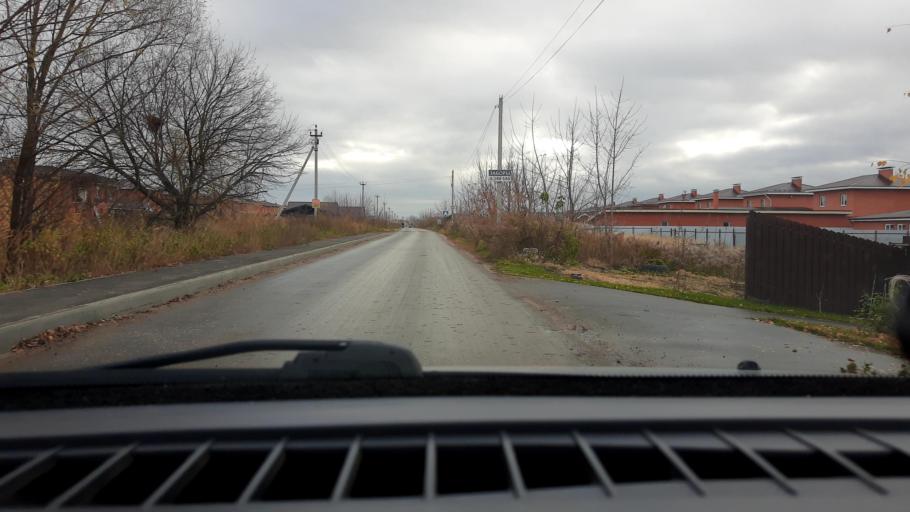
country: RU
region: Nizjnij Novgorod
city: Afonino
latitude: 56.2057
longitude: 44.1271
